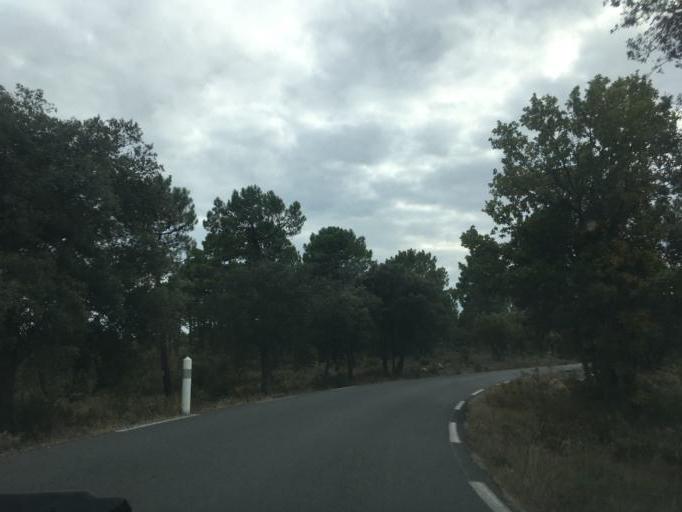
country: FR
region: Provence-Alpes-Cote d'Azur
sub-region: Departement du Var
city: Villecroze
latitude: 43.5515
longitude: 6.3282
